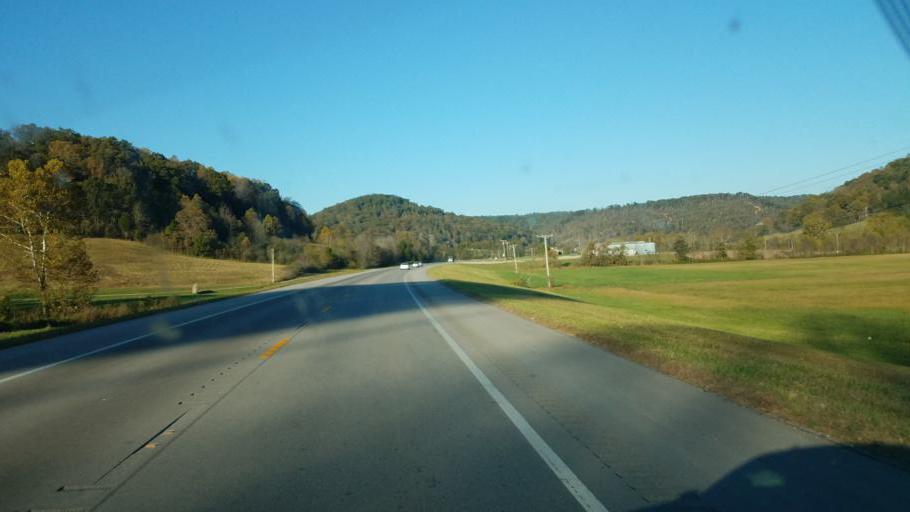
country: US
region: Kentucky
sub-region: Lewis County
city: Vanceburg
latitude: 38.5794
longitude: -83.4271
